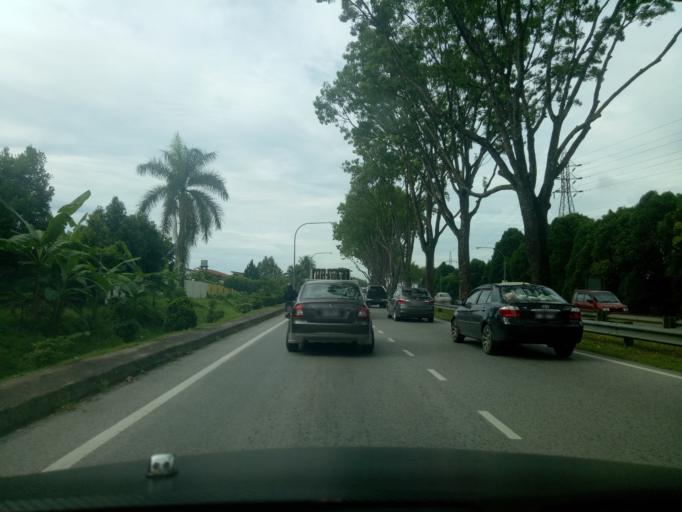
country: MY
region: Sarawak
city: Kuching
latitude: 1.5427
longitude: 110.3719
